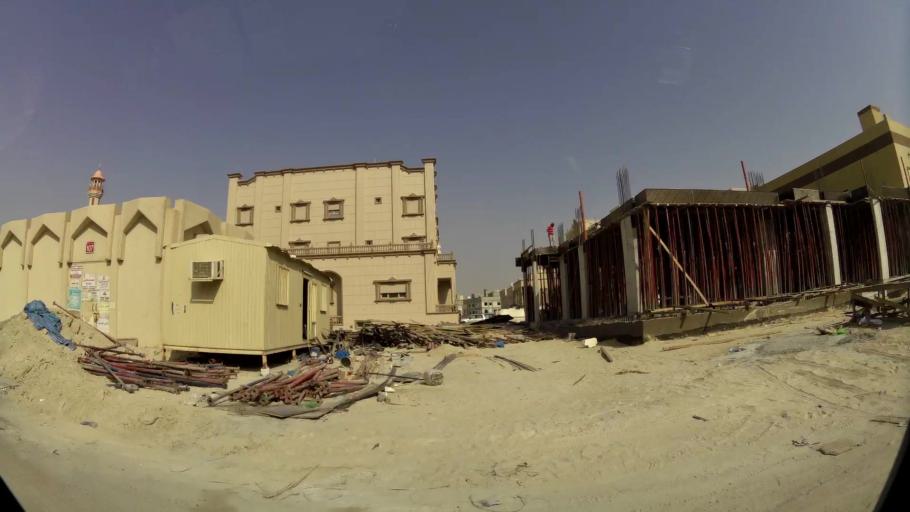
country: KW
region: Muhafazat al Jahra'
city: Al Jahra'
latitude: 29.3537
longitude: 47.7480
